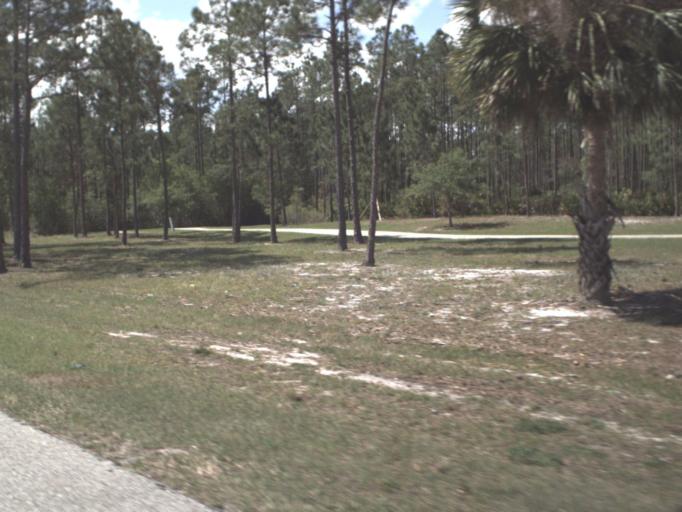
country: US
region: Florida
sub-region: Flagler County
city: Palm Coast
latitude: 29.5716
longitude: -81.2743
